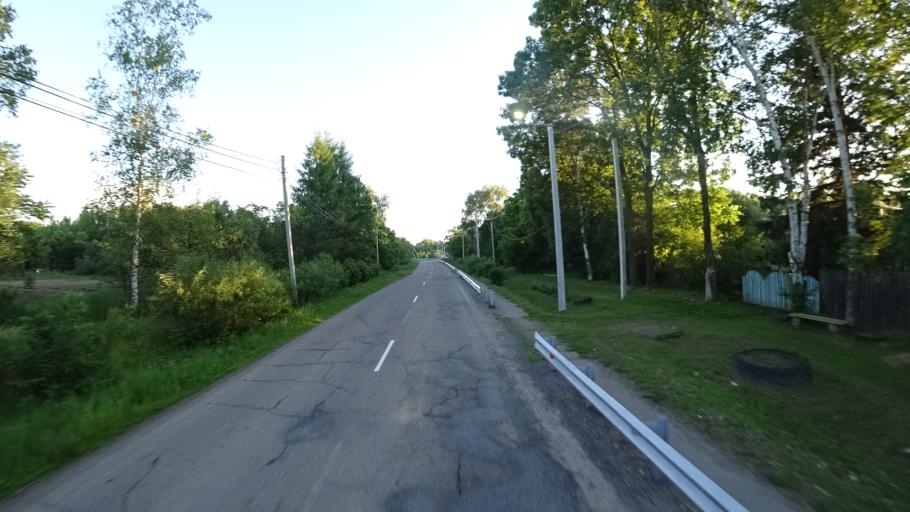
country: RU
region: Khabarovsk Krai
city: Khor
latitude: 47.8542
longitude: 134.9839
